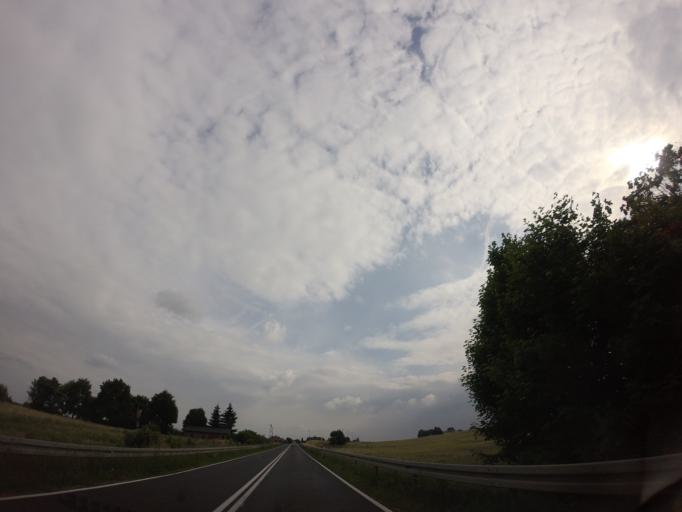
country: PL
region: West Pomeranian Voivodeship
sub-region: Powiat szczecinecki
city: Szczecinek
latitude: 53.6790
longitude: 16.6861
